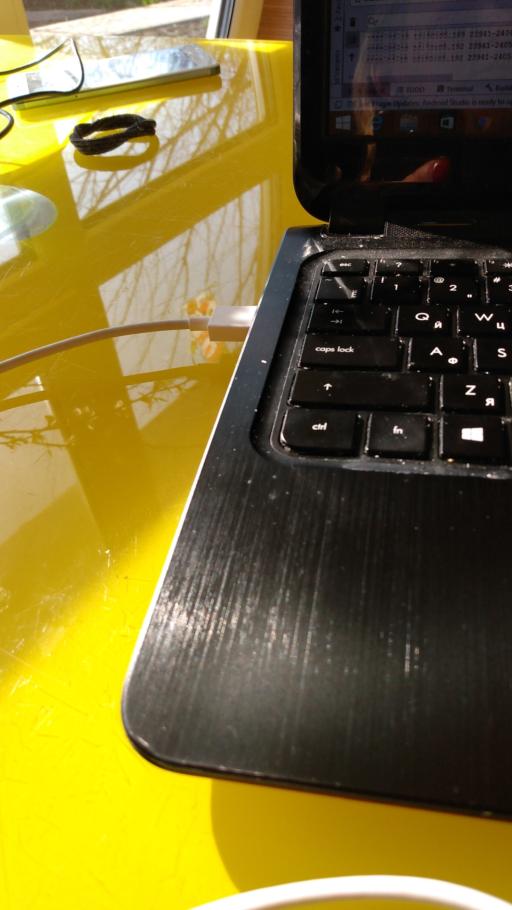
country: RU
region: Novgorod
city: Kresttsy
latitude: 58.4607
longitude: 32.2983
